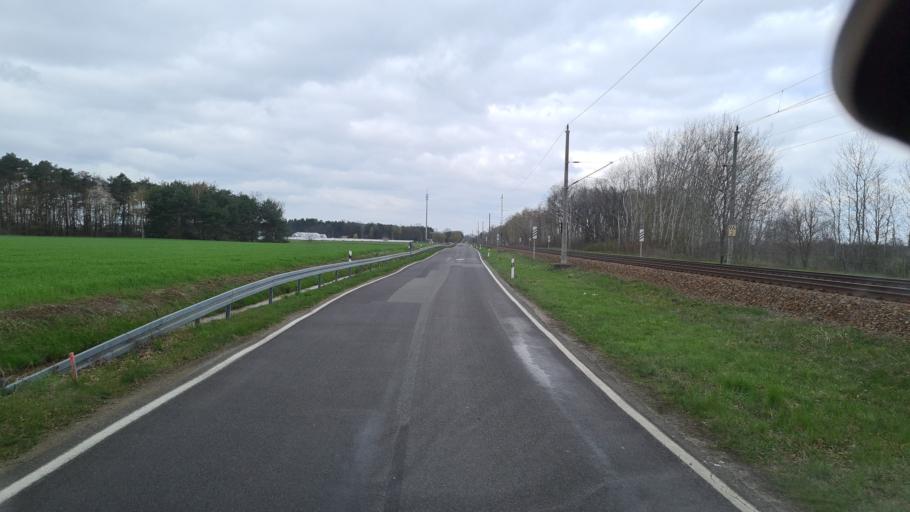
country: DE
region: Brandenburg
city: Ruhland
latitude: 51.4567
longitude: 13.8985
